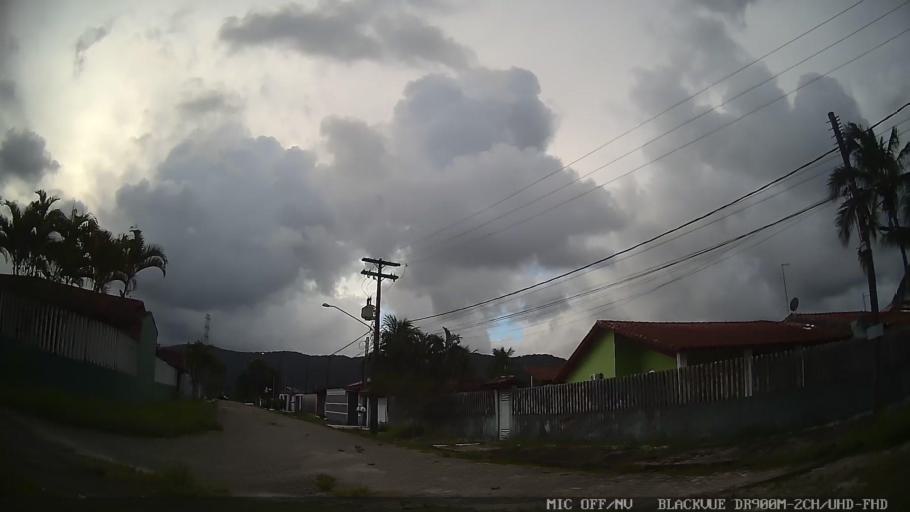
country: BR
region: Sao Paulo
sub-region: Itanhaem
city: Itanhaem
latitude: -24.1519
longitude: -46.7316
